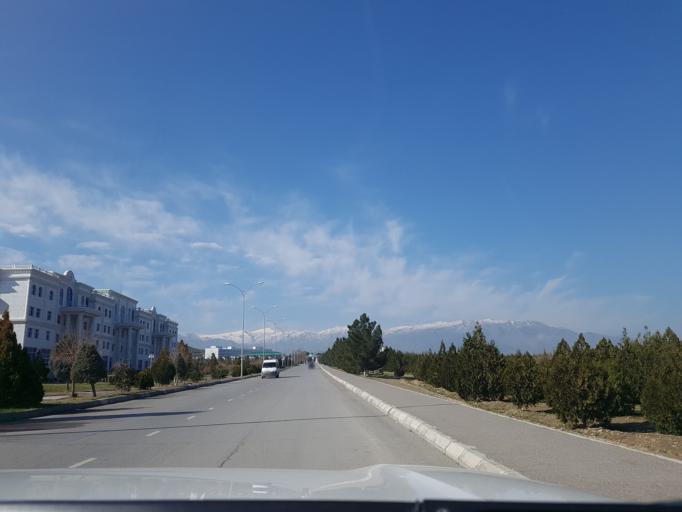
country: TM
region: Ahal
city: Baharly
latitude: 38.5180
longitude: 57.1847
